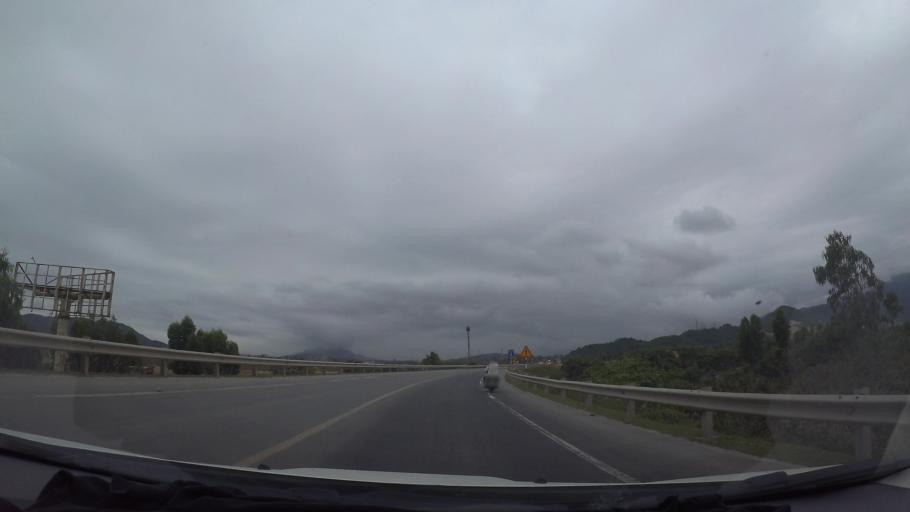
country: VN
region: Da Nang
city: Lien Chieu
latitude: 16.1086
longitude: 108.1047
